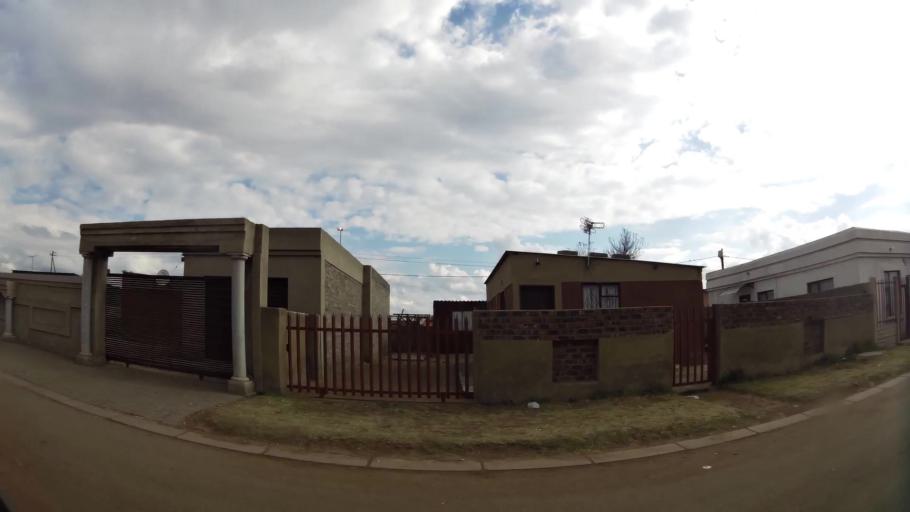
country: ZA
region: Gauteng
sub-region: Sedibeng District Municipality
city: Vanderbijlpark
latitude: -26.6877
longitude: 27.7800
